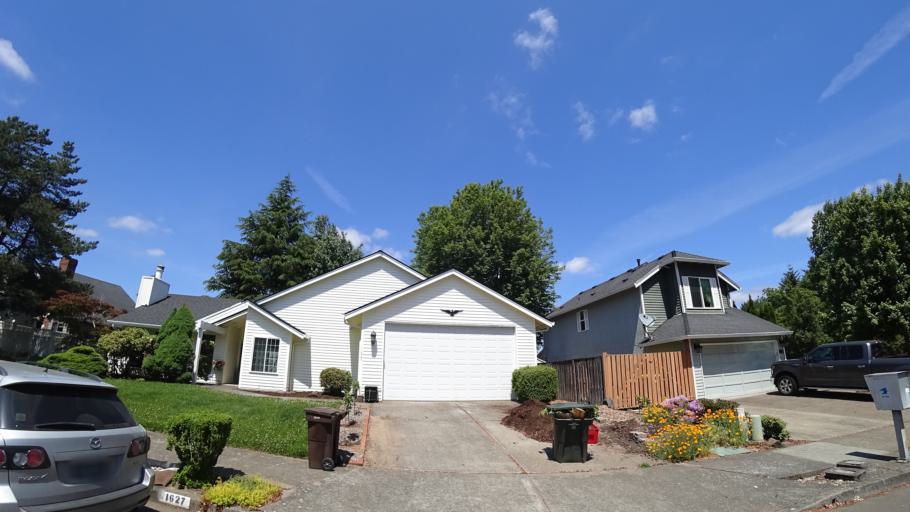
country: US
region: Oregon
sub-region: Washington County
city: Tigard
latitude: 45.4408
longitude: -122.7961
